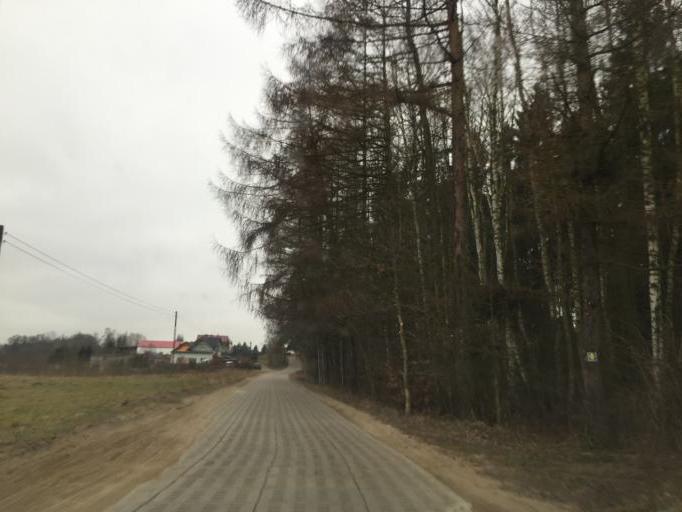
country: PL
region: Pomeranian Voivodeship
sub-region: Powiat kartuski
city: Banino
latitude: 54.3836
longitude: 18.4202
